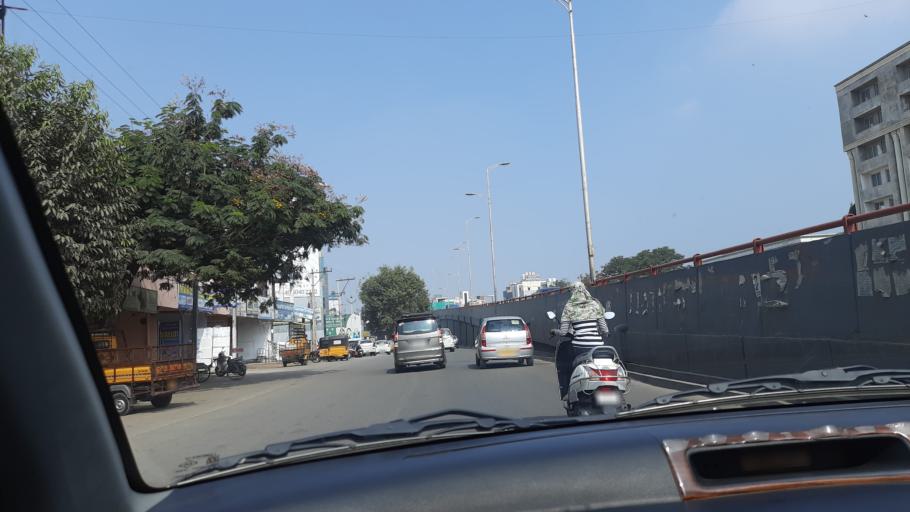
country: IN
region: Telangana
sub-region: Rangareddi
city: Lal Bahadur Nagar
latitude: 17.3511
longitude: 78.5543
